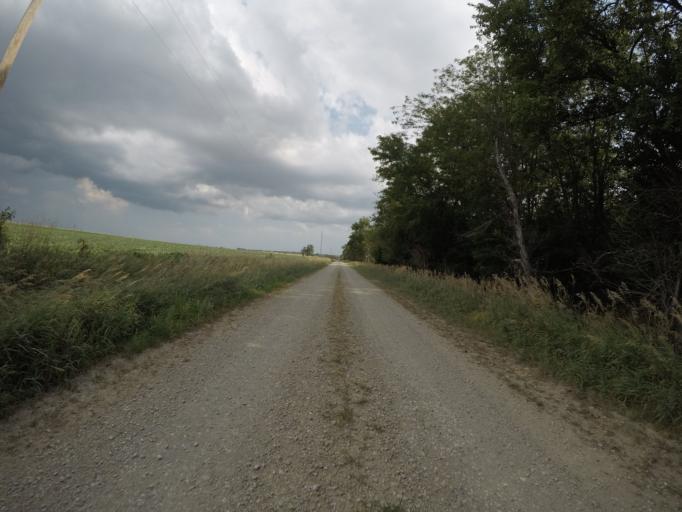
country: US
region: Kansas
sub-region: Marshall County
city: Blue Rapids
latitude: 39.5331
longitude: -96.8291
